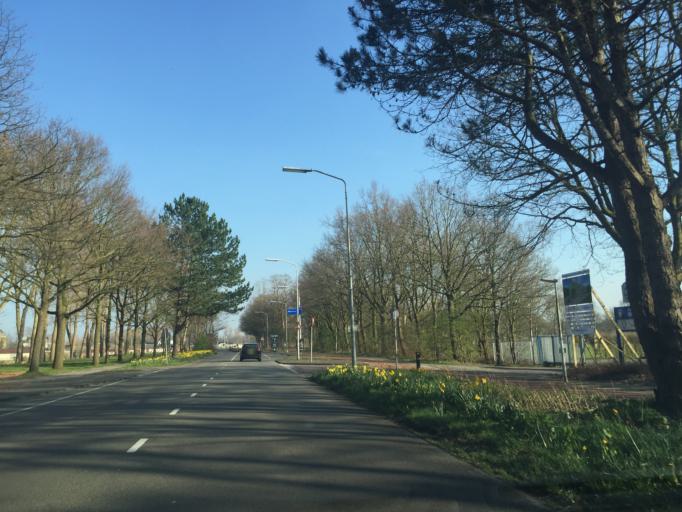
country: NL
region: South Holland
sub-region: Gemeente Oegstgeest
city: Oegstgeest
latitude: 52.1782
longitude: 4.4840
